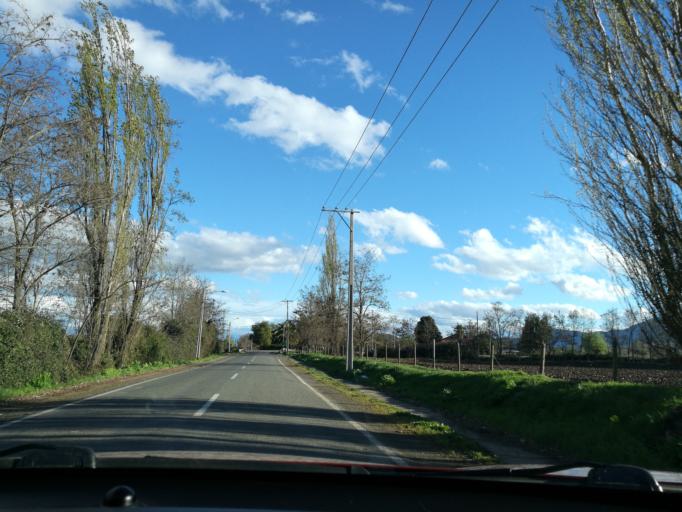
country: CL
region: O'Higgins
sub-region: Provincia de Cachapoal
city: Graneros
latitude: -34.1068
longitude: -70.8096
